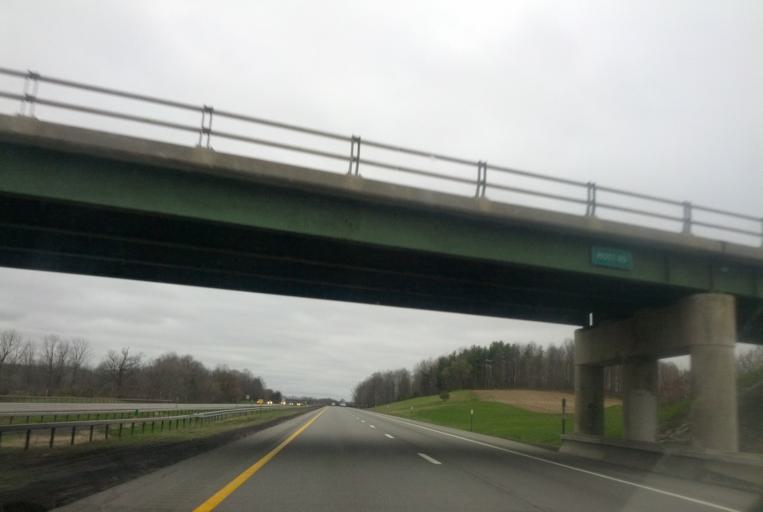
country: US
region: New York
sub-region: Ontario County
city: Phelps
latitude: 42.9620
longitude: -77.0421
